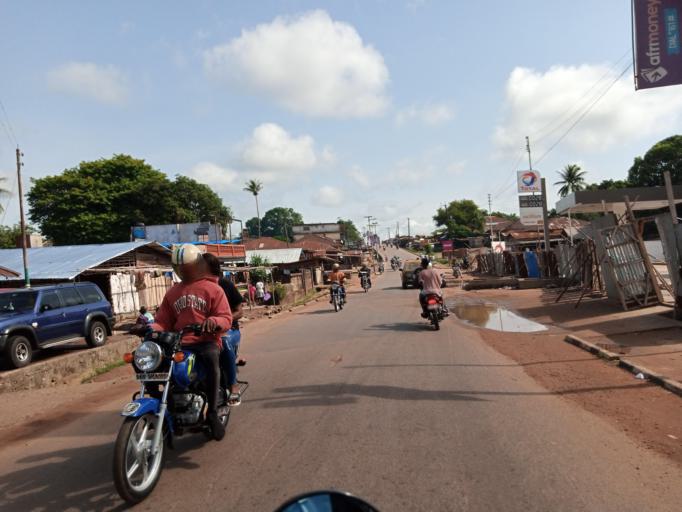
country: SL
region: Southern Province
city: Bo
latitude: 7.9600
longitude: -11.7334
